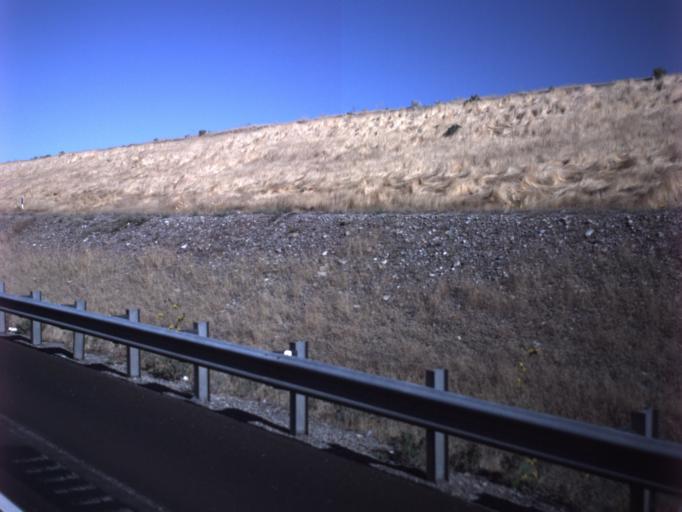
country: US
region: Utah
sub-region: Salt Lake County
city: Magna
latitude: 40.7204
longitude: -112.1497
